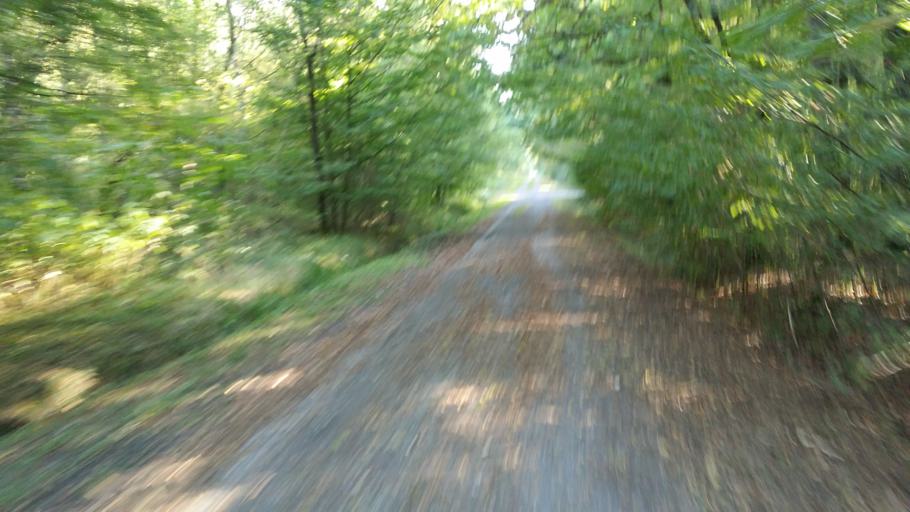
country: DE
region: Hesse
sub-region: Regierungsbezirk Giessen
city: Giessen
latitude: 50.5764
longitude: 8.7243
